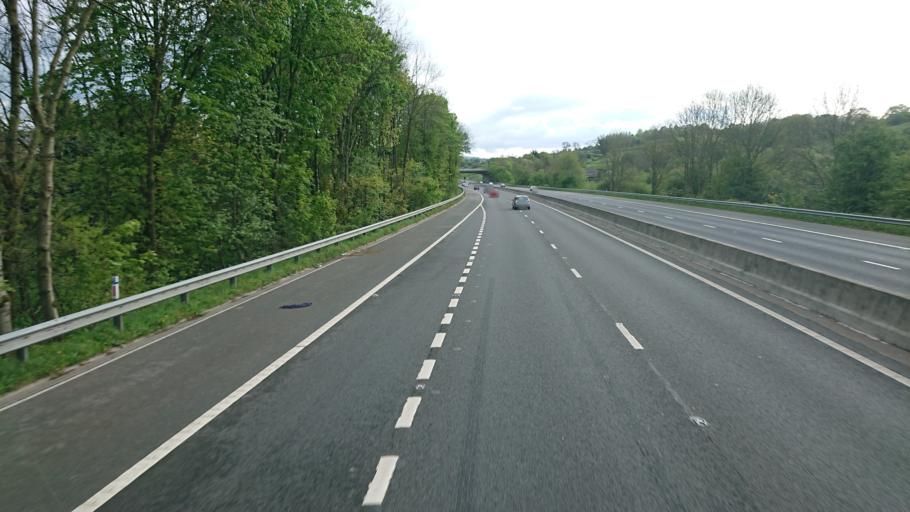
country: GB
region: England
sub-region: Lancashire
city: Brierfield
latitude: 53.8270
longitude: -2.2415
